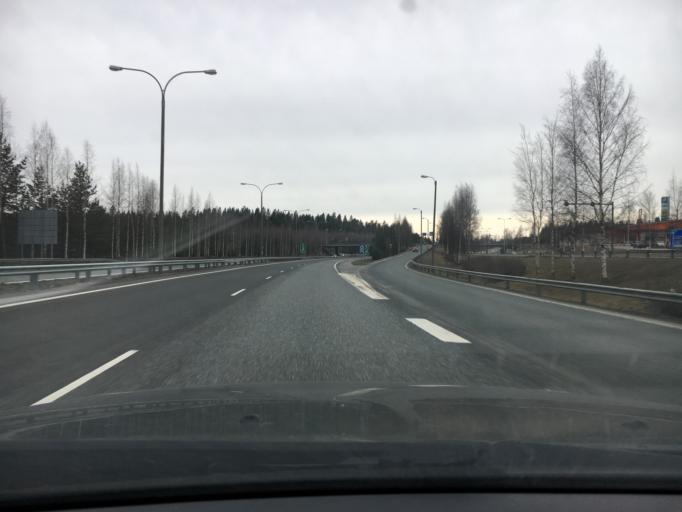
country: FI
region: Northern Savo
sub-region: Kuopio
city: Siilinjaervi
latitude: 63.0710
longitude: 27.6580
